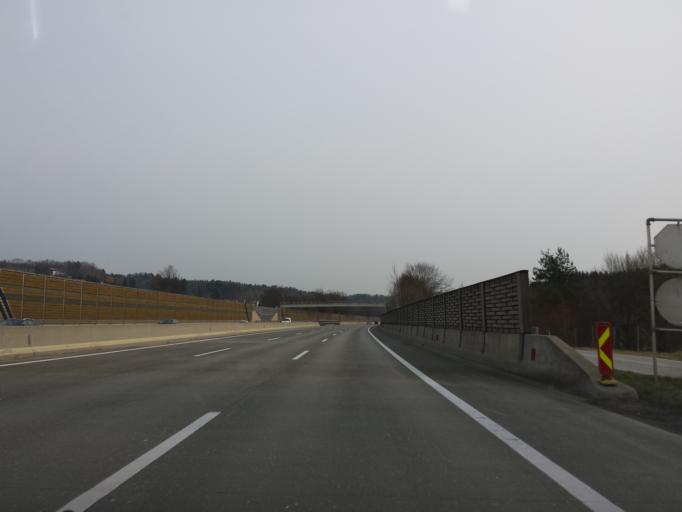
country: AT
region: Styria
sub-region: Politischer Bezirk Weiz
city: Ungerdorf
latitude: 47.0800
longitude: 15.6464
